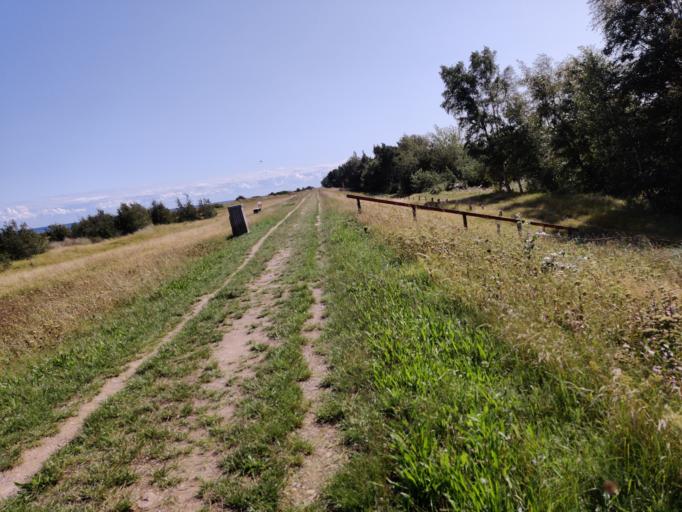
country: DK
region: Zealand
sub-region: Guldborgsund Kommune
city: Nykobing Falster
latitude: 54.6003
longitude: 11.9680
